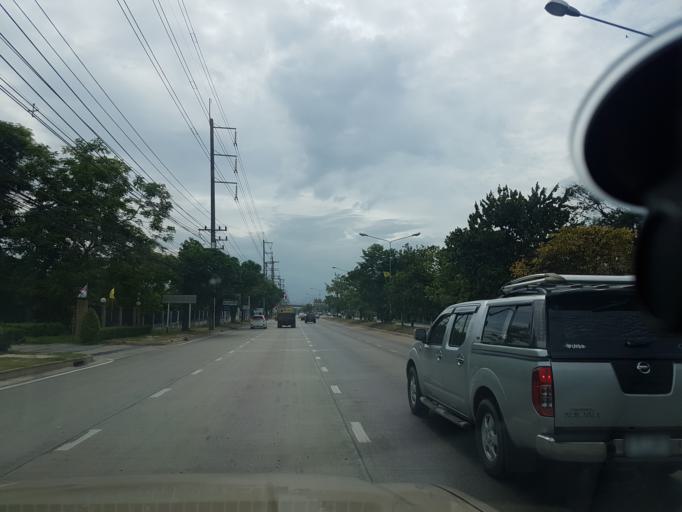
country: TH
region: Sara Buri
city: Phra Phutthabat
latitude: 14.7216
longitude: 100.8048
